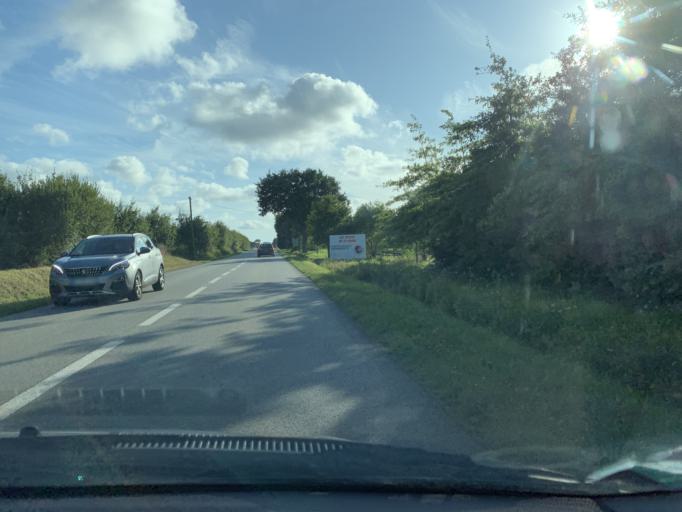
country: FR
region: Brittany
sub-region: Departement du Morbihan
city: Sarzeau
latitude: 47.5549
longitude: -2.7037
